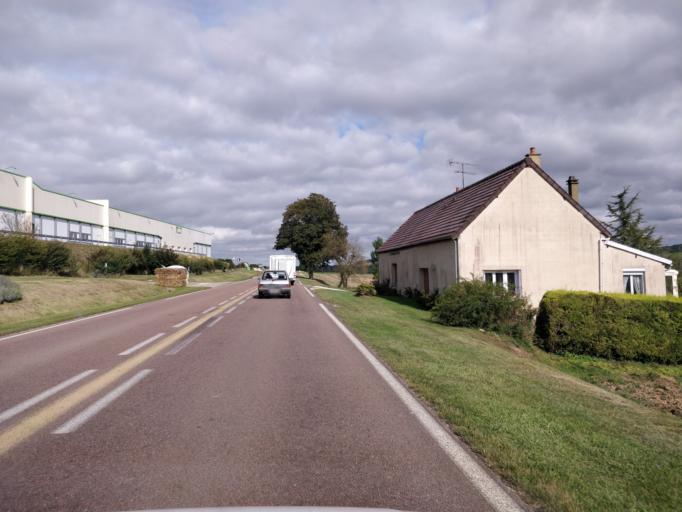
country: FR
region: Champagne-Ardenne
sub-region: Departement de l'Aube
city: Aix-en-Othe
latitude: 48.2368
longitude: 3.6766
